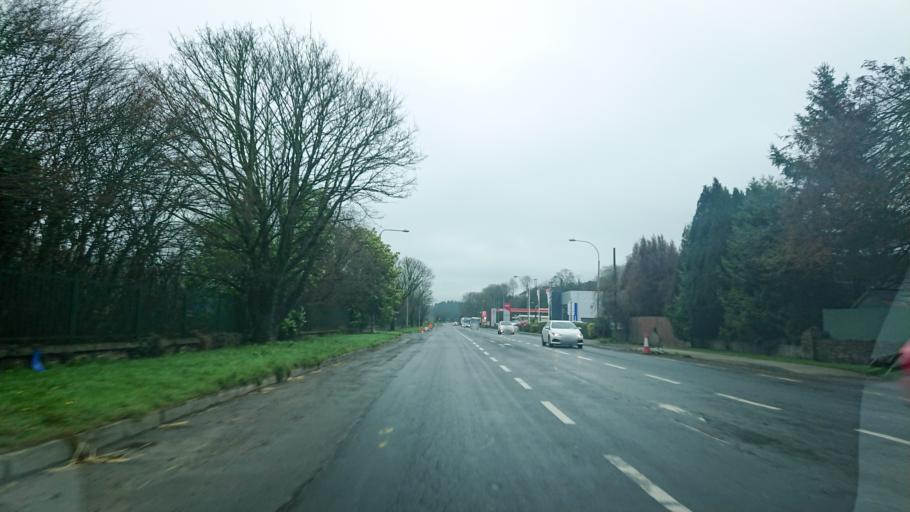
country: IE
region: Munster
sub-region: County Cork
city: Bandon
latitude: 51.7510
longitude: -8.7189
